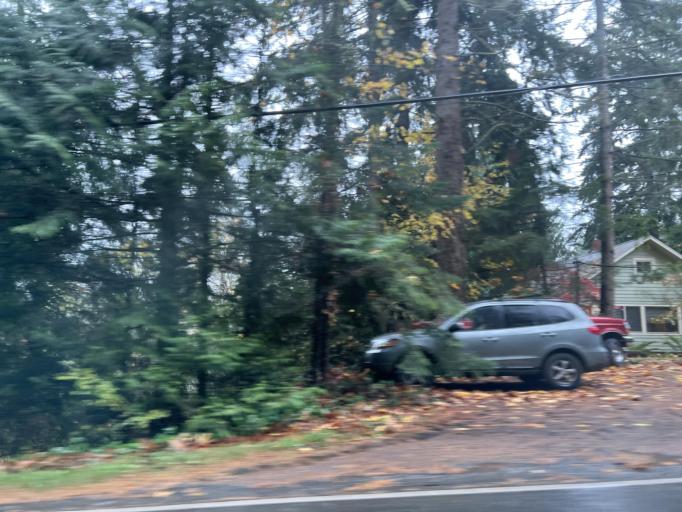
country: US
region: Washington
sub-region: Kitsap County
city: Bainbridge Island
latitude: 47.6586
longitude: -122.5210
